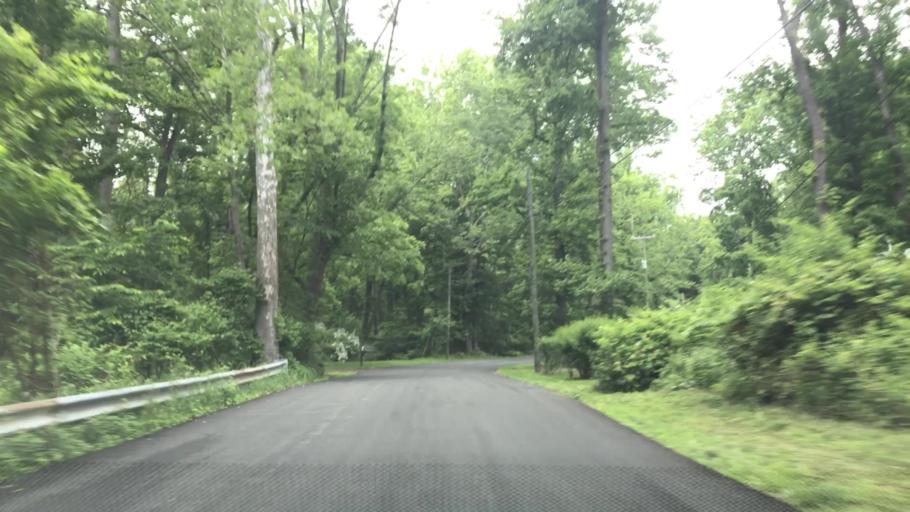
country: US
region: New Jersey
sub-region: Hunterdon County
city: Lebanon
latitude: 40.6611
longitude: -74.8334
